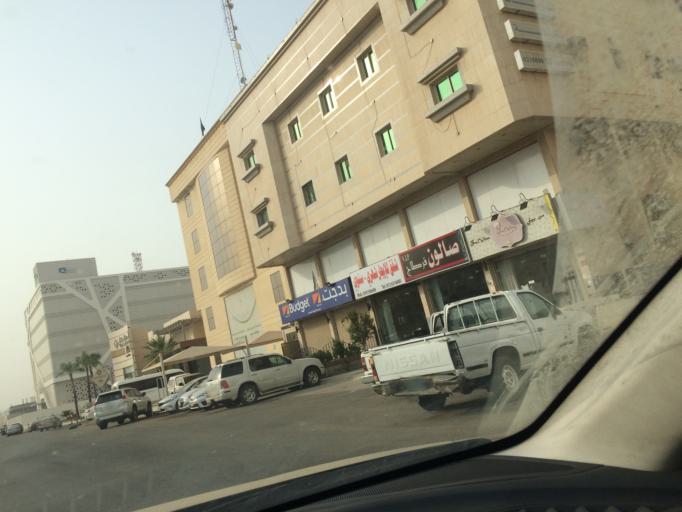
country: SA
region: Makkah
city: Jeddah
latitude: 21.4881
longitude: 39.2265
